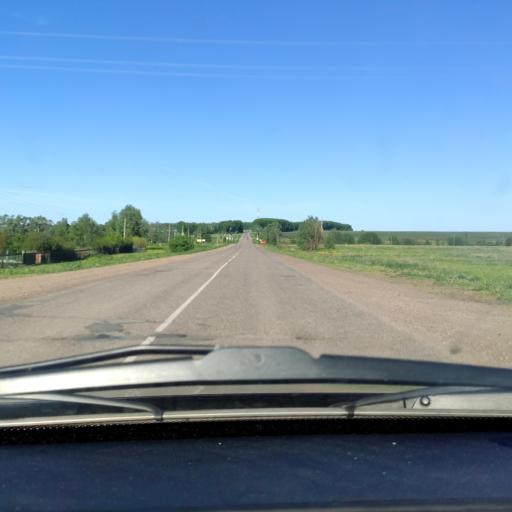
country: RU
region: Bashkortostan
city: Asanovo
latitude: 54.8101
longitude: 55.5745
